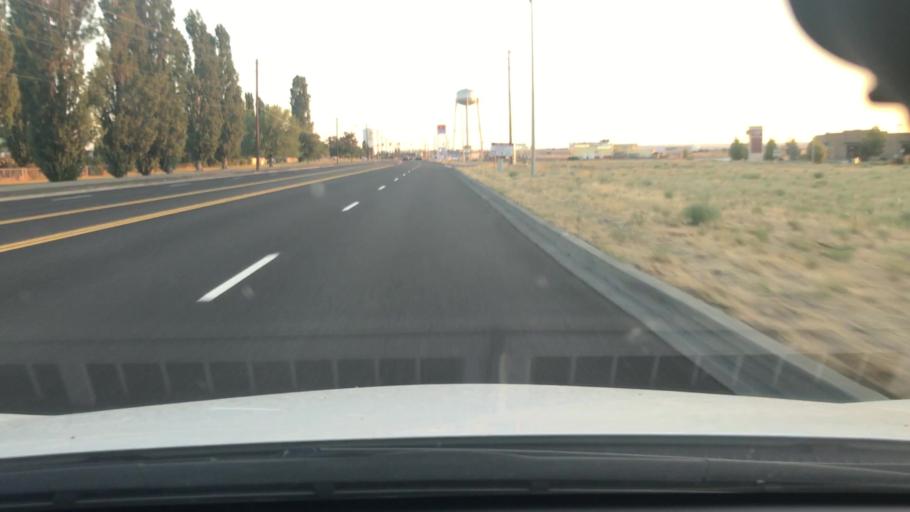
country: US
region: Washington
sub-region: Grant County
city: Cascade Valley
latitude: 47.1609
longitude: -119.3122
